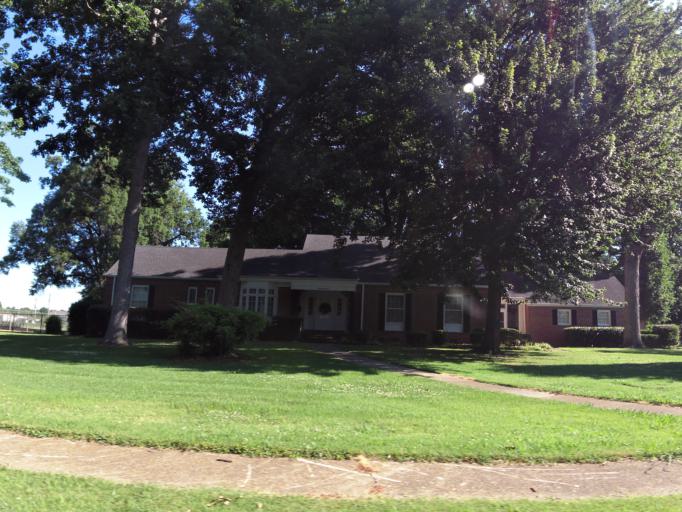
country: US
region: Arkansas
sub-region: Clay County
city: Corning
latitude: 36.4087
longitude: -90.5903
